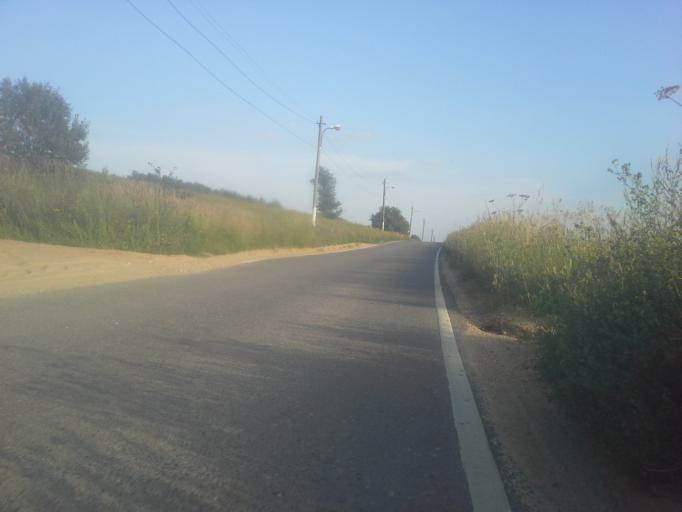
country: RU
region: Moskovskaya
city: Nikolina Gora
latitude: 55.7436
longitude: 36.9867
